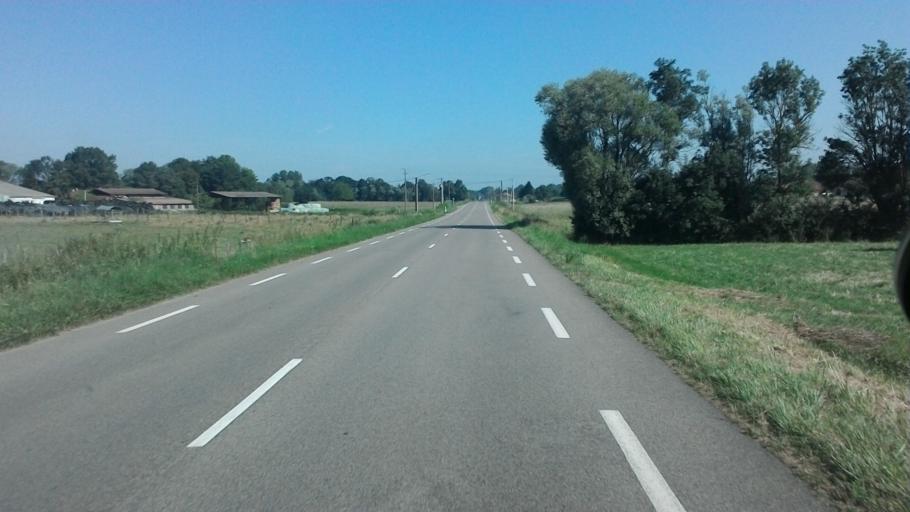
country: FR
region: Rhone-Alpes
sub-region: Departement de l'Ain
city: Montrevel-en-Bresse
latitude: 46.3870
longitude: 5.1167
